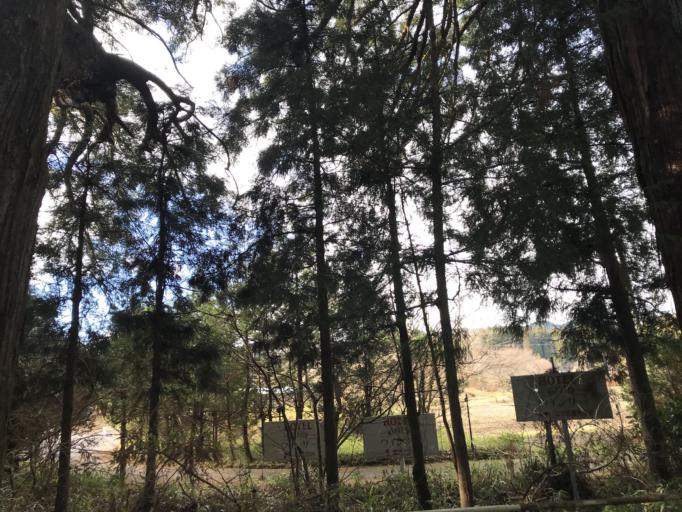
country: JP
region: Tochigi
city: Imaichi
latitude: 36.6893
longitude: 139.7173
